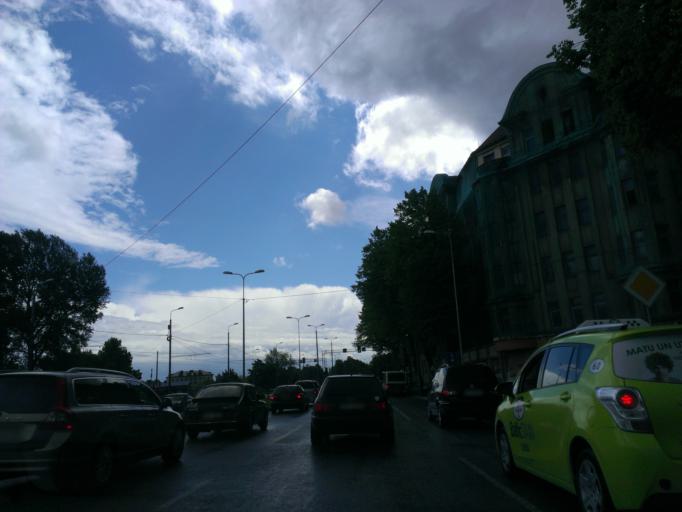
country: LV
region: Riga
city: Riga
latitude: 56.9458
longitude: 24.0831
